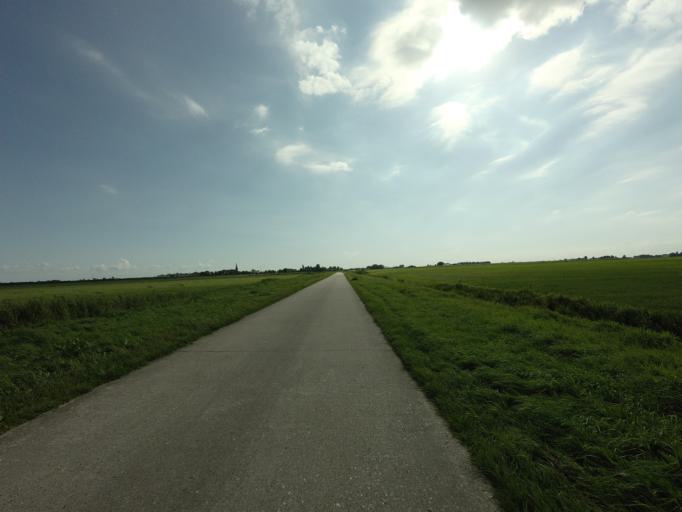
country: NL
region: Friesland
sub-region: Gemeente Littenseradiel
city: Makkum
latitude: 53.0845
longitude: 5.6322
